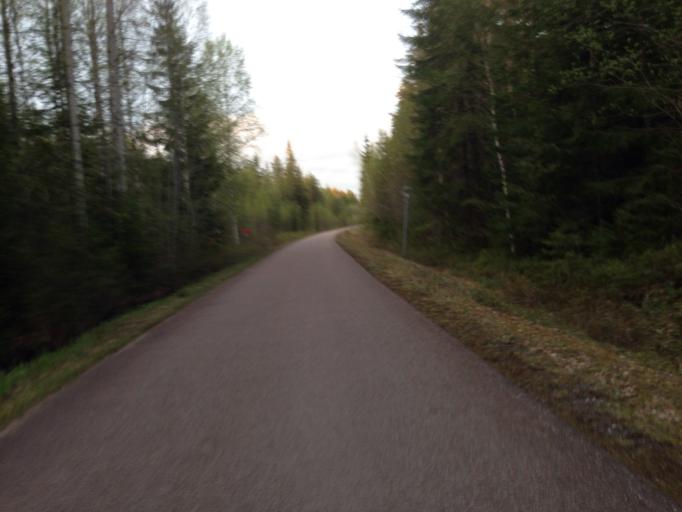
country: SE
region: Dalarna
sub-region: Ludvika Kommun
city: Grangesberg
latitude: 60.1382
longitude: 15.0784
